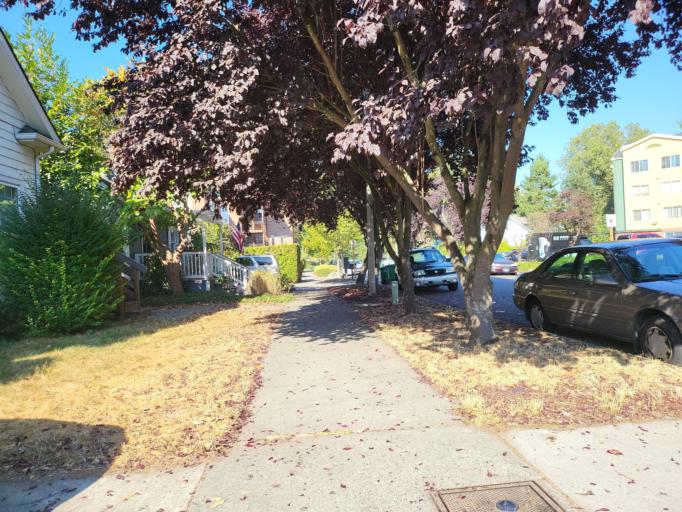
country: US
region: Washington
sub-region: King County
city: Renton
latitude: 47.4818
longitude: -122.2043
